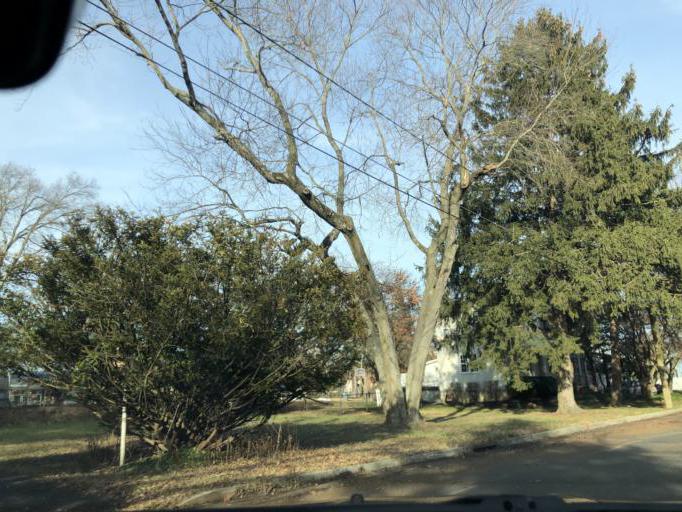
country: US
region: New Jersey
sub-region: Burlington County
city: Maple Shade
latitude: 39.9563
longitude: -74.9810
